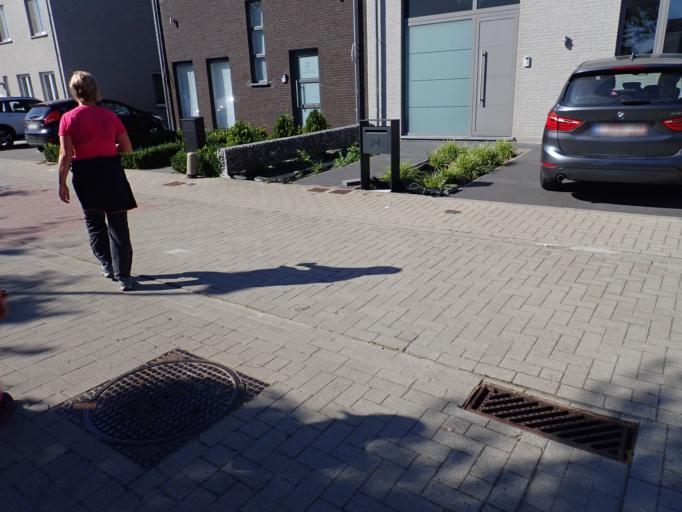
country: BE
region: Flanders
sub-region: Provincie Oost-Vlaanderen
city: Hamme
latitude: 51.0889
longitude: 4.1545
